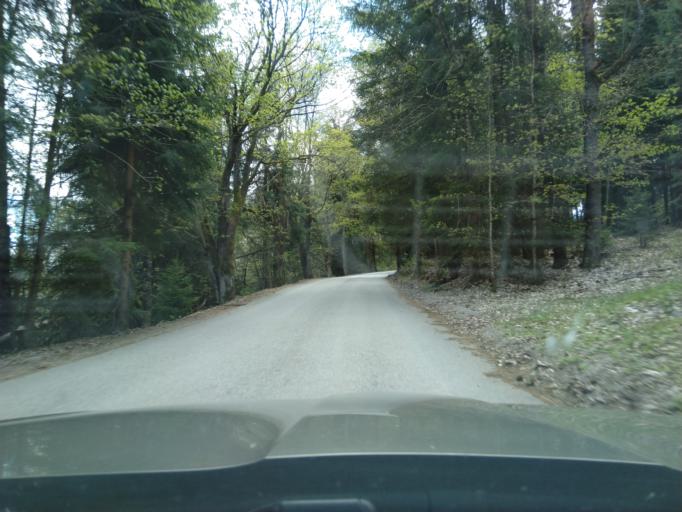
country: CZ
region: Jihocesky
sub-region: Okres Prachatice
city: Vimperk
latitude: 49.0159
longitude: 13.7267
